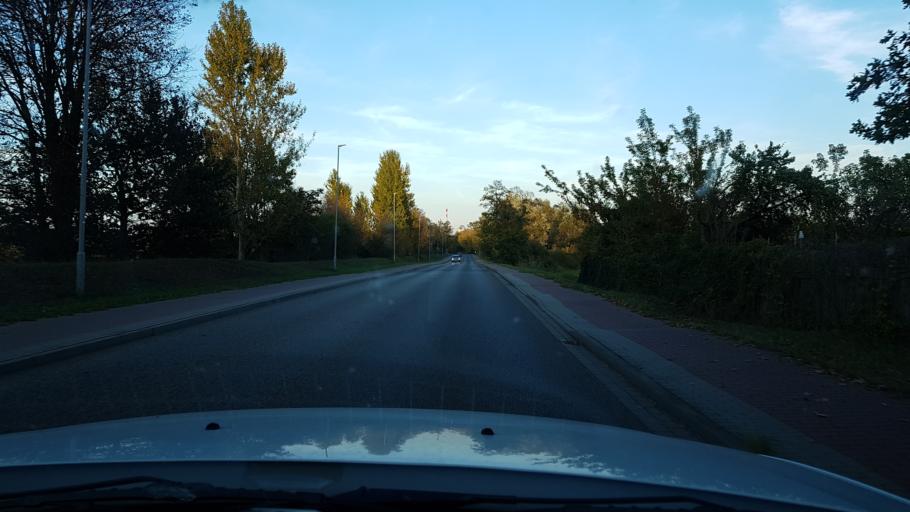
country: DE
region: Brandenburg
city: Schwedt (Oder)
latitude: 53.0736
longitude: 14.3047
